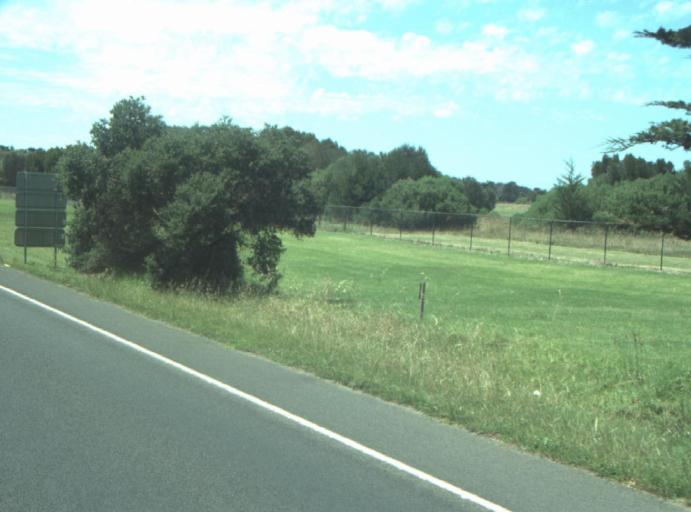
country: AU
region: Victoria
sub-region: Greater Geelong
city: Leopold
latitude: -38.2671
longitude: 144.4602
